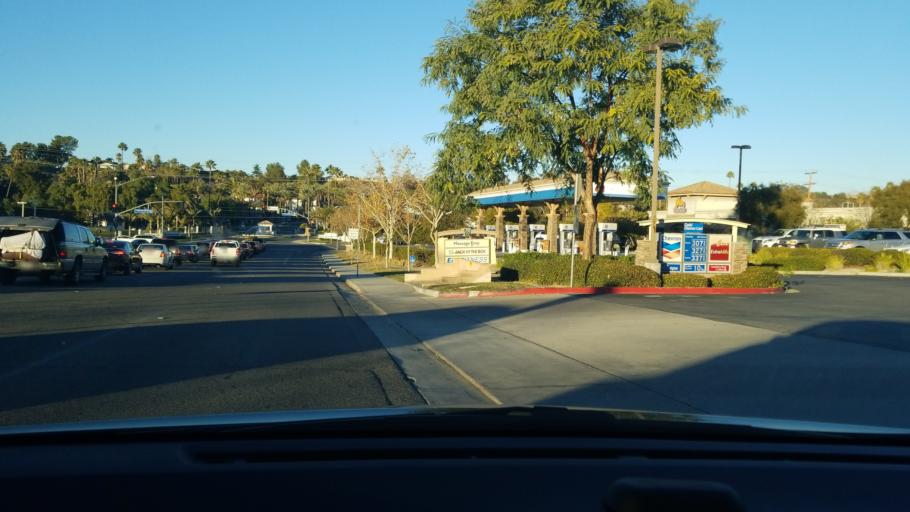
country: US
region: California
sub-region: Riverside County
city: Murrieta Hot Springs
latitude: 33.5554
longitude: -117.1574
